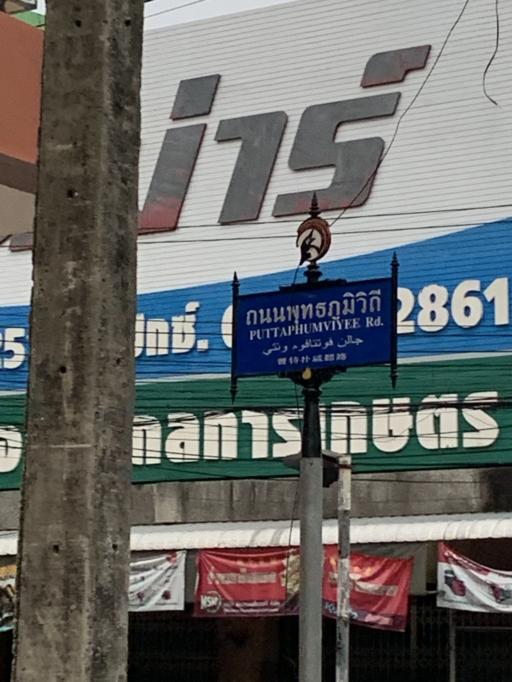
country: TH
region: Yala
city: Yala
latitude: 6.5565
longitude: 101.2902
